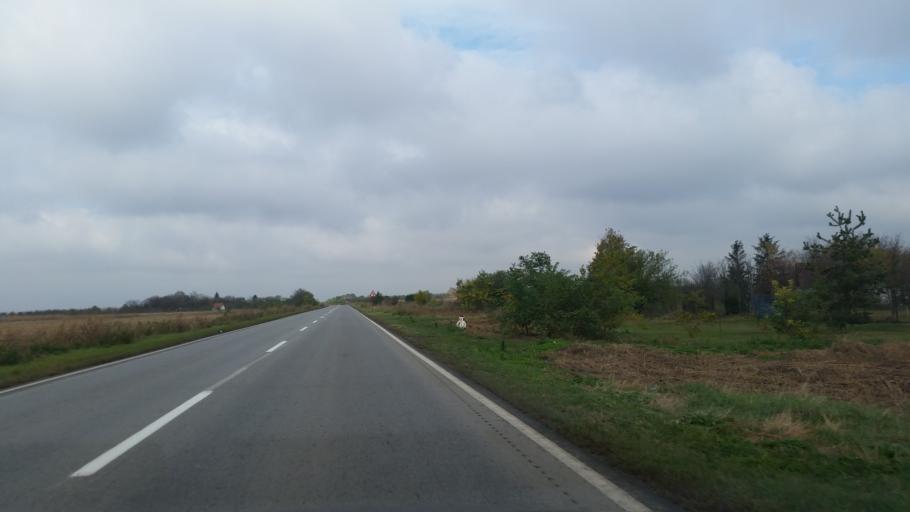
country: RS
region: Autonomna Pokrajina Vojvodina
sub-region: Srednjebanatski Okrug
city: Zrenjanin
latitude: 45.4338
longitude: 20.3669
